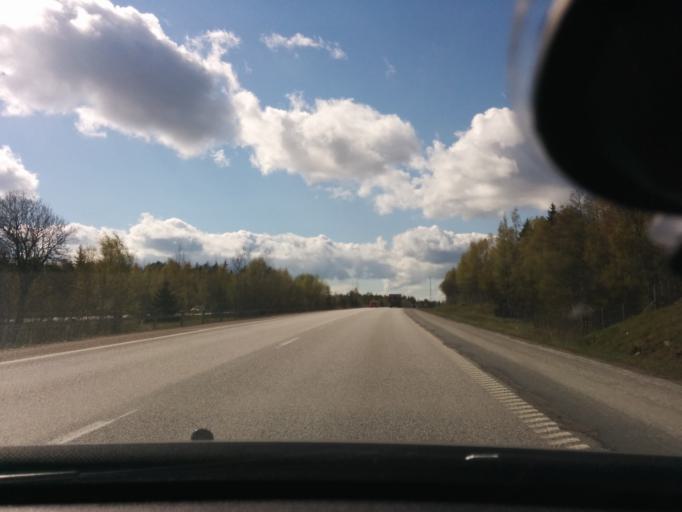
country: SE
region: Stockholm
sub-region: Upplands-Bro Kommun
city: Kungsaengen
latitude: 59.5097
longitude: 17.7013
